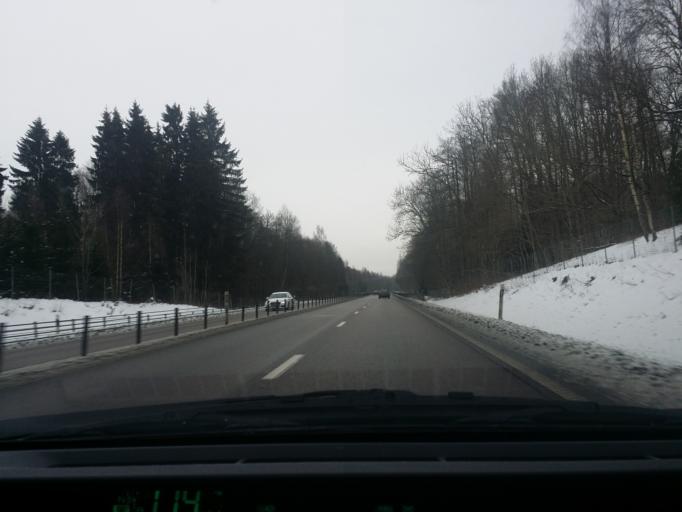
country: SE
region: Vaestra Goetaland
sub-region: Skovde Kommun
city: Stopen
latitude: 58.4961
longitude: 13.8456
